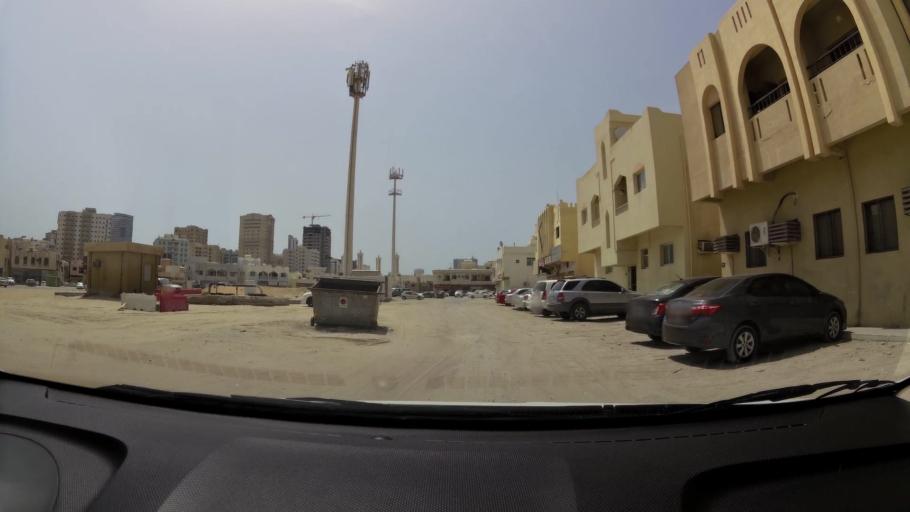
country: AE
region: Ash Shariqah
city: Sharjah
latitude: 25.3481
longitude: 55.4010
